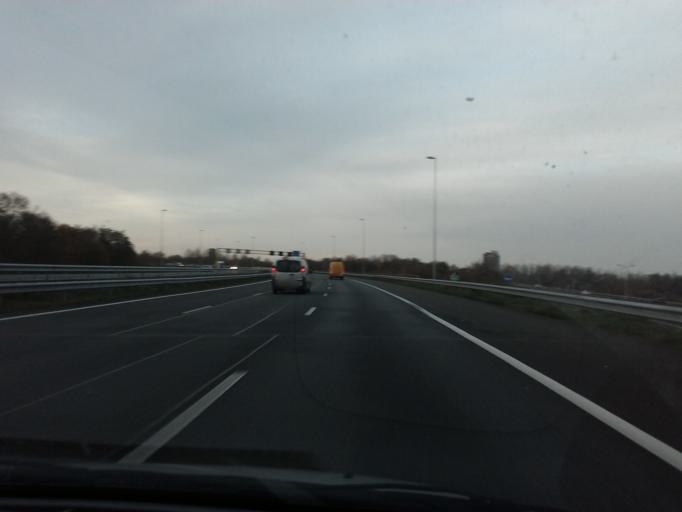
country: NL
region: North Brabant
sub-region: Gemeente Vught
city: Vught
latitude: 51.6681
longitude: 5.3079
